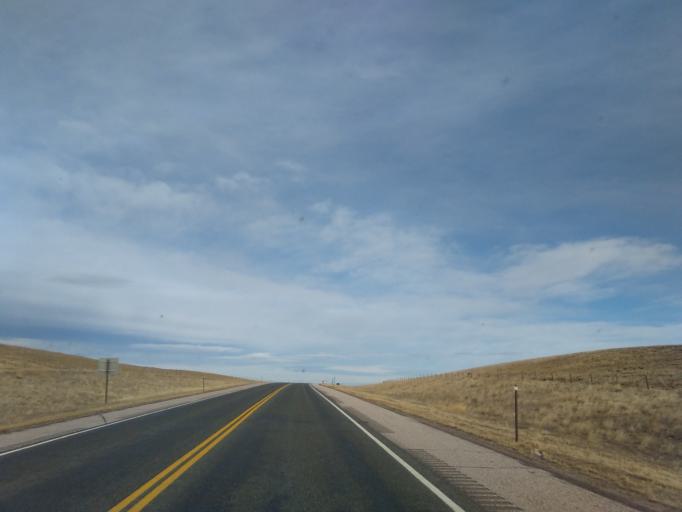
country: US
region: Wyoming
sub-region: Laramie County
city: Pine Bluffs
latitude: 41.5945
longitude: -104.2657
